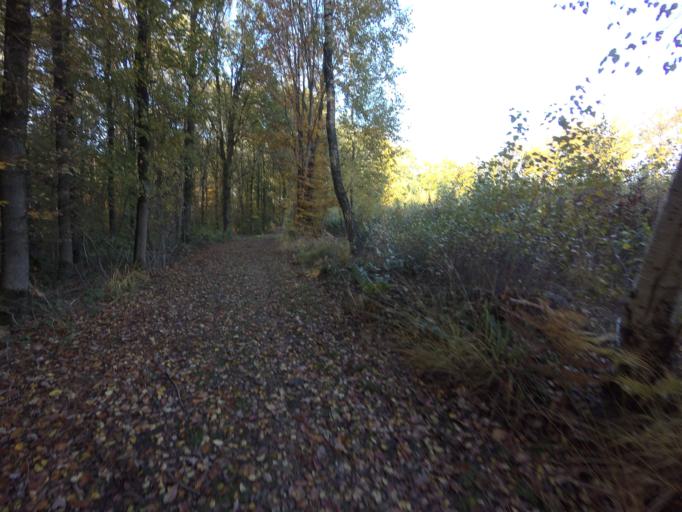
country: BE
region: Wallonia
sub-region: Province de Liege
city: Plombieres
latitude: 50.7792
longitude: 5.9402
